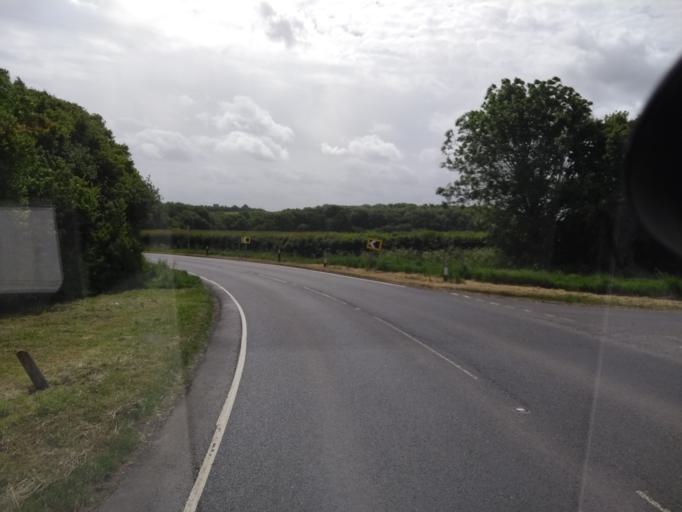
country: GB
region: England
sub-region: Somerset
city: Bridgwater
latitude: 51.1780
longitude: -3.1060
